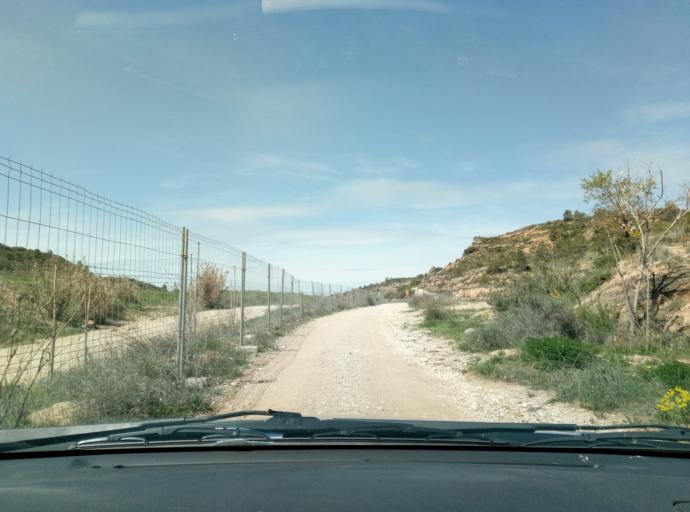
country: ES
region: Catalonia
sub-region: Provincia de Lleida
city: Juncosa
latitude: 41.4425
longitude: 0.8042
